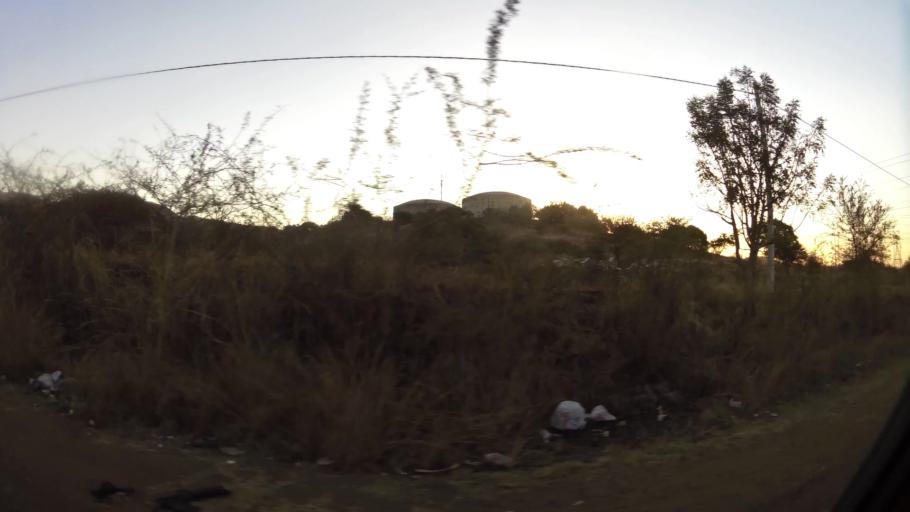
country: ZA
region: North-West
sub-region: Bojanala Platinum District Municipality
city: Rustenburg
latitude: -25.6328
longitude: 27.2024
